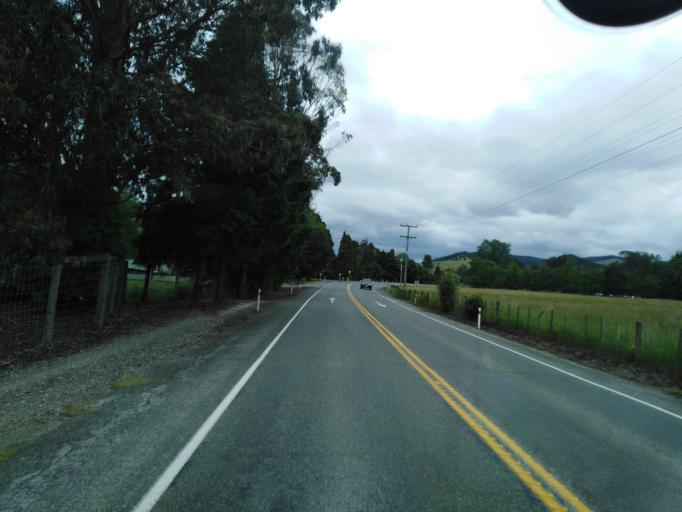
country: NZ
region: Tasman
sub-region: Tasman District
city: Wakefield
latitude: -41.4532
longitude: 172.9572
